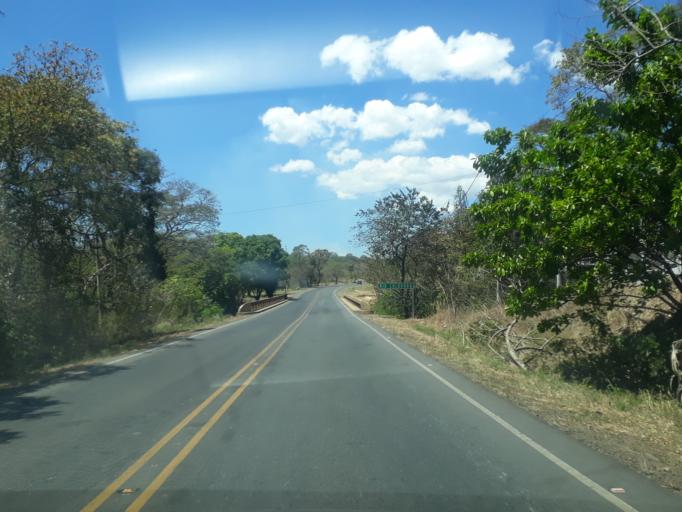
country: CR
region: Guanacaste
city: Liberia
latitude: 10.6687
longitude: -85.4806
